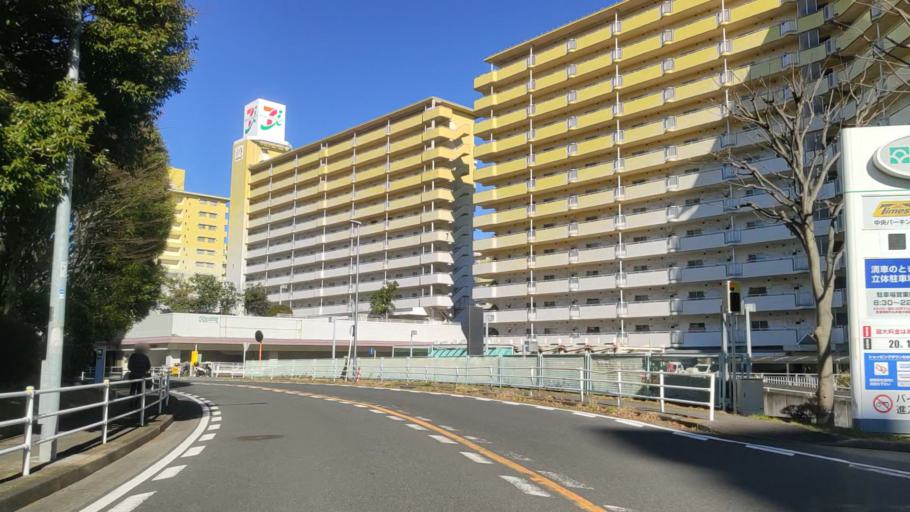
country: JP
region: Kanagawa
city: Minami-rinkan
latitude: 35.5042
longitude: 139.4972
